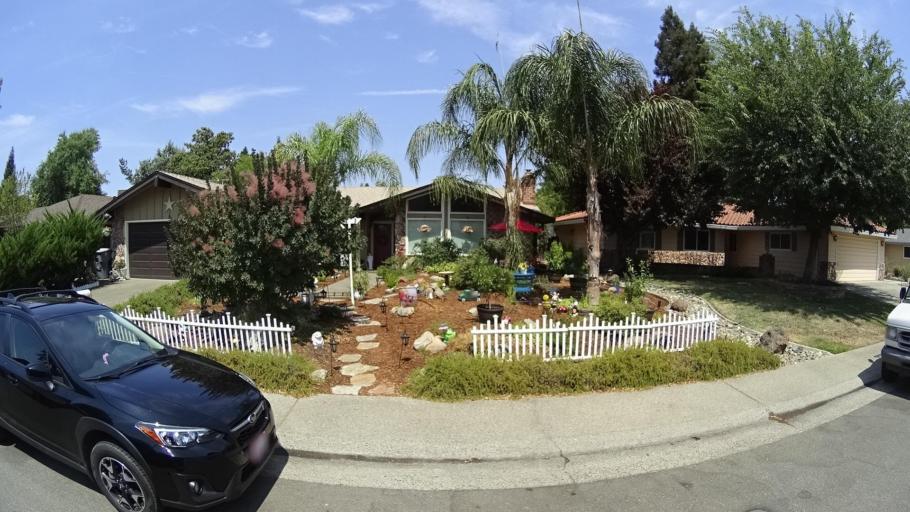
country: US
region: California
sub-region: Placer County
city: Rocklin
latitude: 38.7981
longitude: -121.2354
